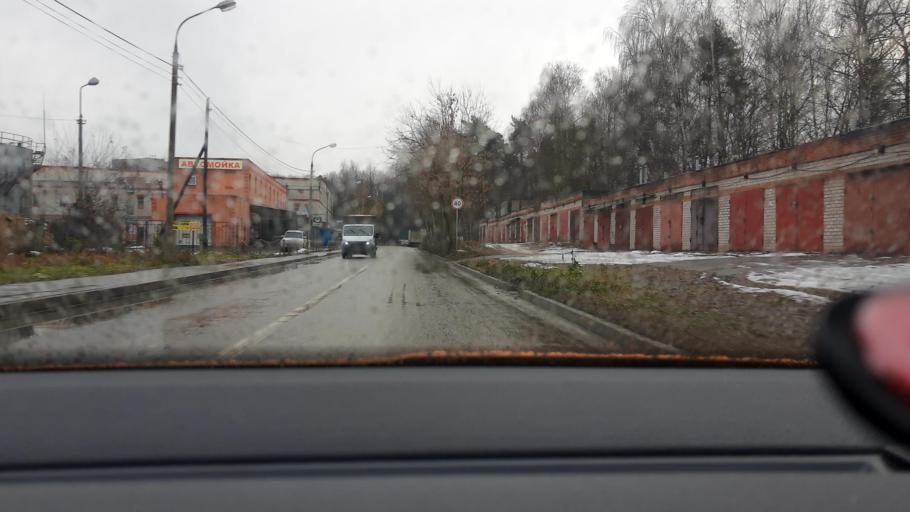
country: RU
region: Moskovskaya
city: Bolshevo
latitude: 55.9304
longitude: 37.8259
